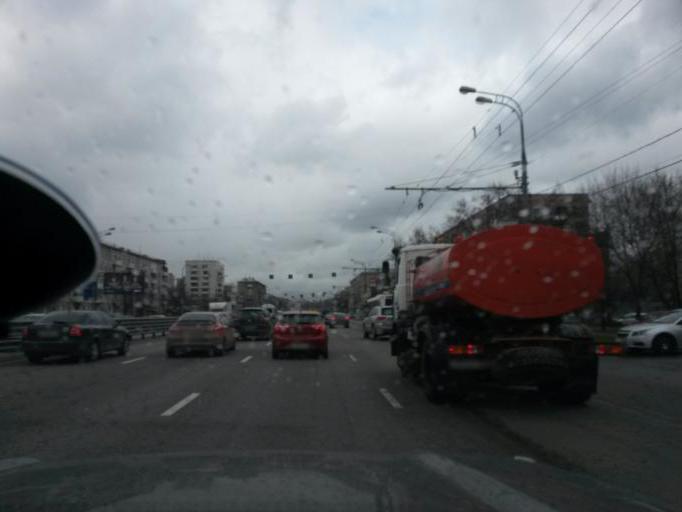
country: RU
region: Moscow
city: Nagornyy
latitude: 55.6514
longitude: 37.6197
